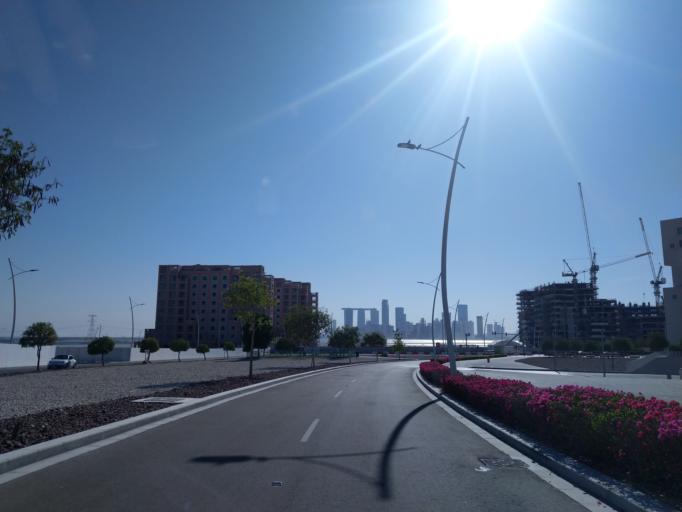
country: AE
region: Abu Dhabi
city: Abu Dhabi
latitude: 24.5230
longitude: 54.4373
